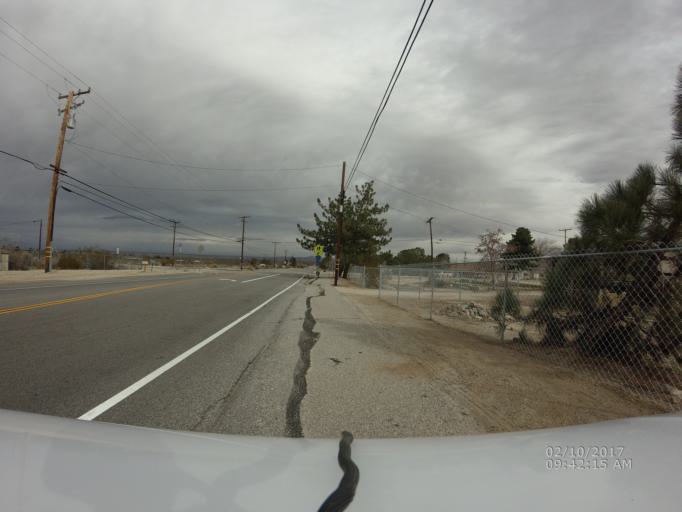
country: US
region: California
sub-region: Los Angeles County
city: Littlerock
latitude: 34.4988
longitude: -117.8965
